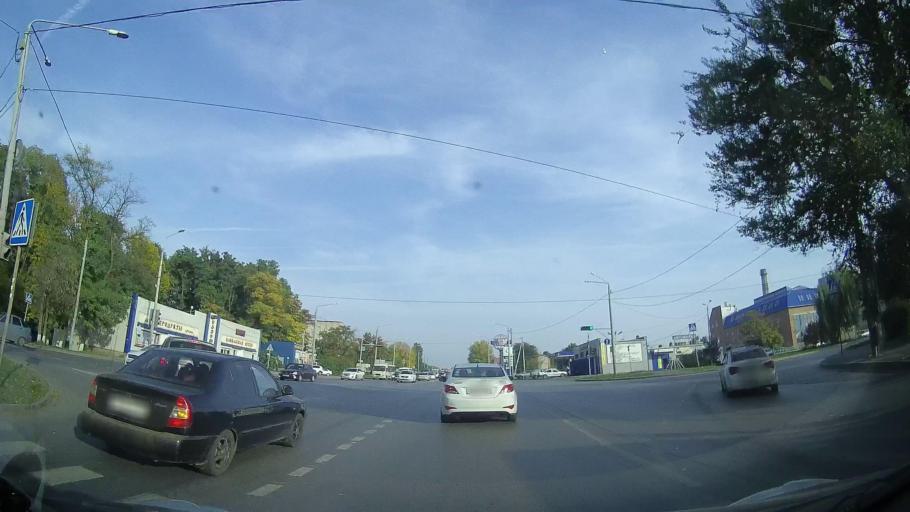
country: RU
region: Rostov
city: Imeni Chkalova
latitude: 47.2801
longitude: 39.7681
